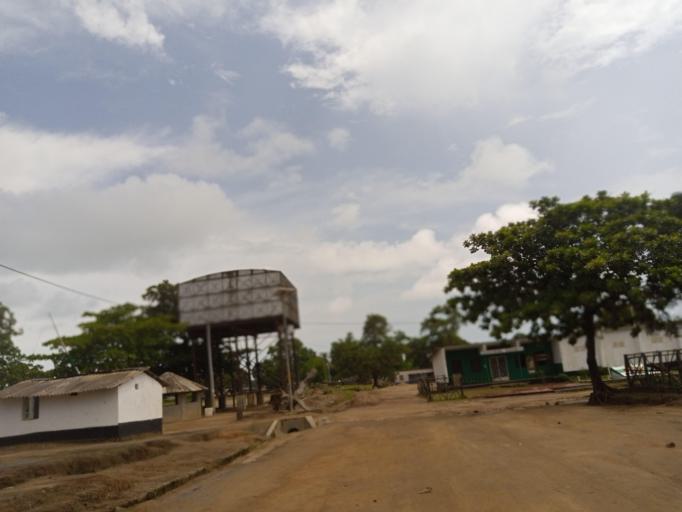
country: SL
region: Northern Province
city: Sawkta
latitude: 8.6270
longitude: -13.2071
